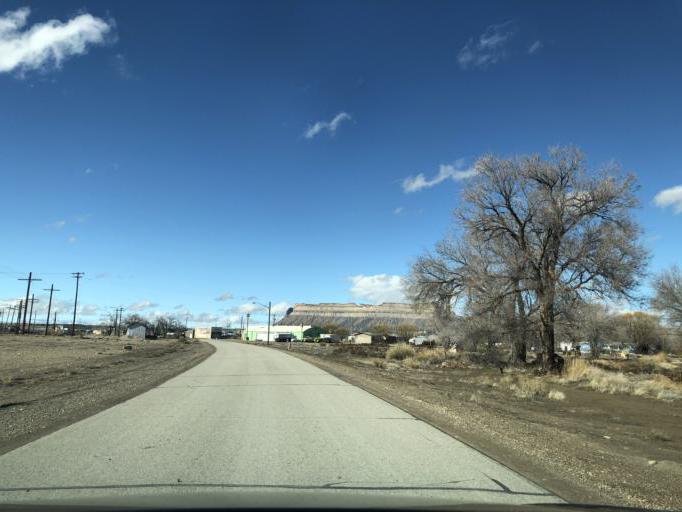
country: US
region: Utah
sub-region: Carbon County
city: East Carbon City
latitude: 38.9915
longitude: -110.1627
